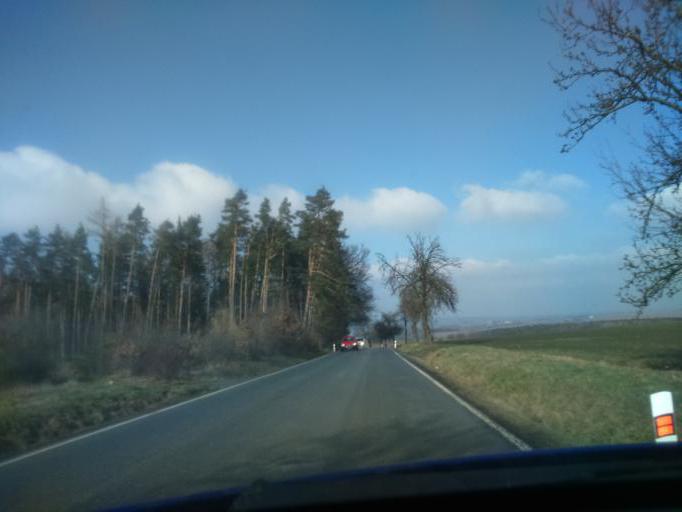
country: CZ
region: Plzensky
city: Horsovsky Tyn
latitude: 49.4941
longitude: 12.9456
